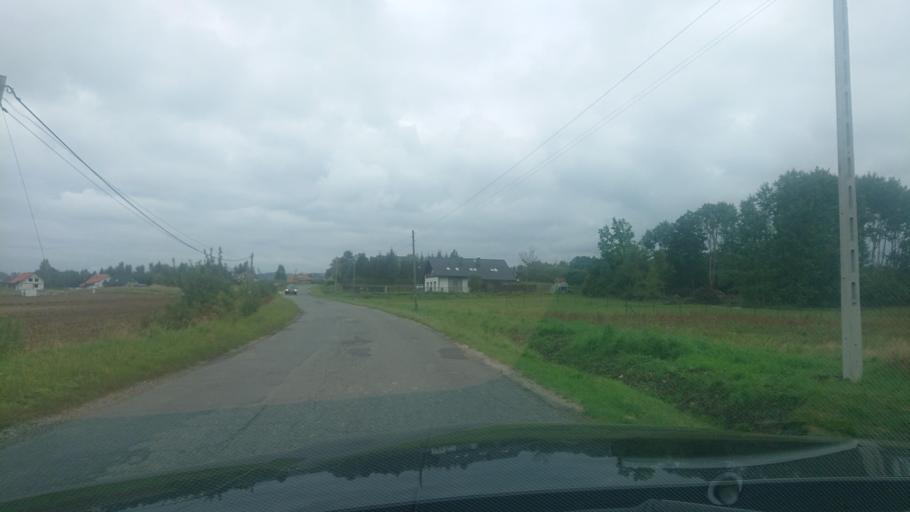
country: PL
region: Lower Silesian Voivodeship
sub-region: Powiat klodzki
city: Bystrzyca Klodzka
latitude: 50.3084
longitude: 16.6671
